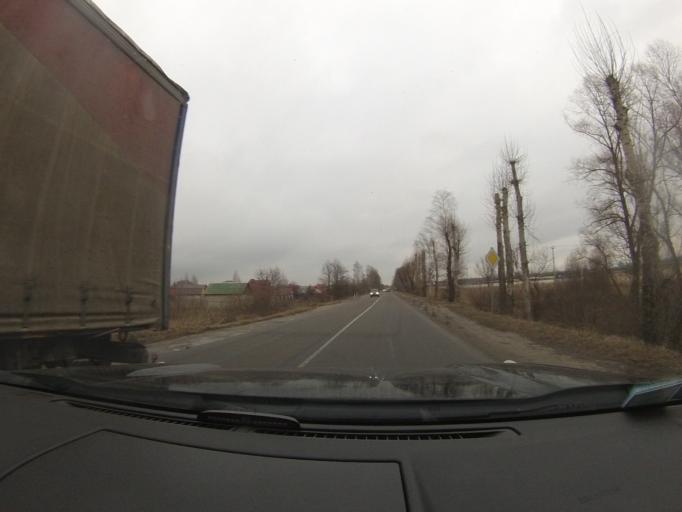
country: RU
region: Moskovskaya
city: Lopatinskiy
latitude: 55.3290
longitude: 38.7218
